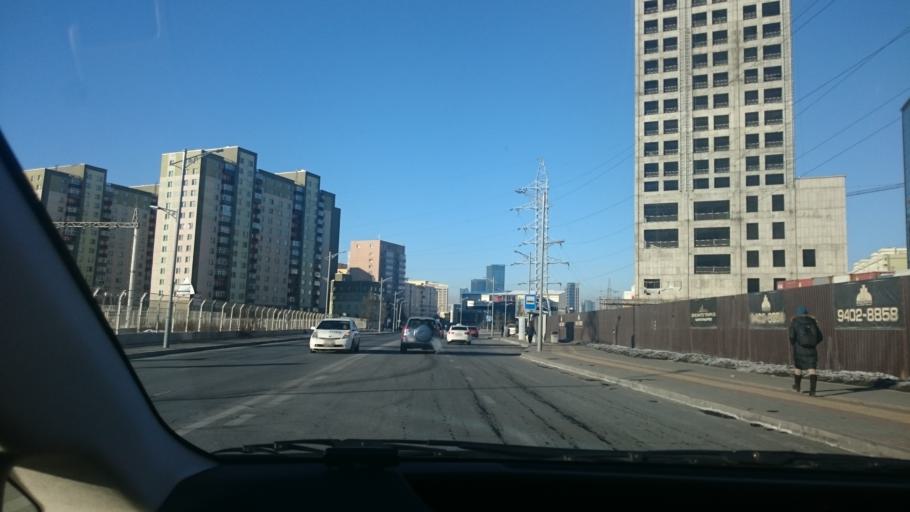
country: MN
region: Ulaanbaatar
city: Ulaanbaatar
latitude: 47.9015
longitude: 106.9294
